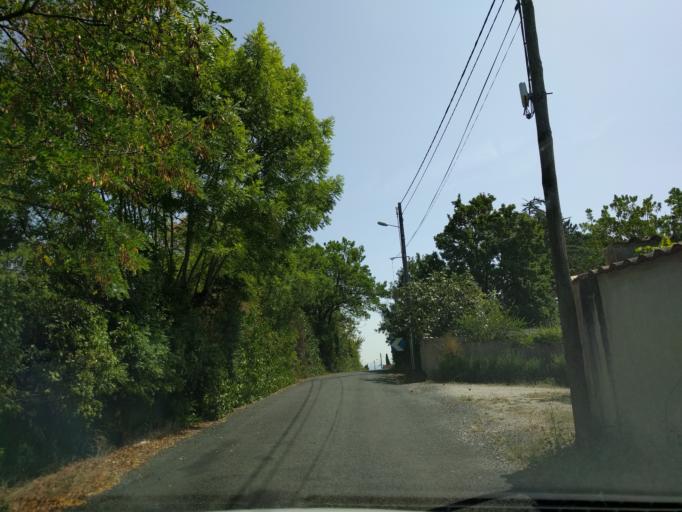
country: FR
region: Midi-Pyrenees
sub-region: Departement du Tarn
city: Castres
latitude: 43.5958
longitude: 2.2564
